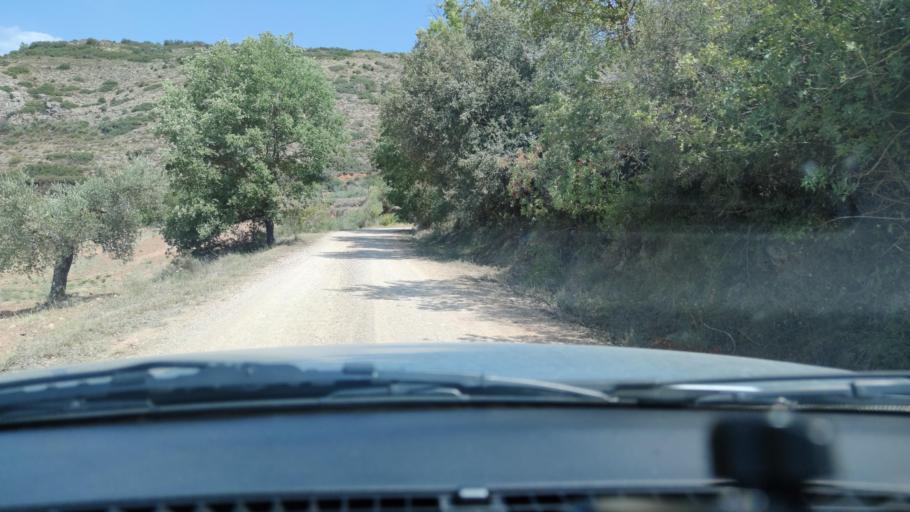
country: ES
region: Catalonia
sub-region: Provincia de Lleida
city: Ager
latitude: 41.9307
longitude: 0.8064
